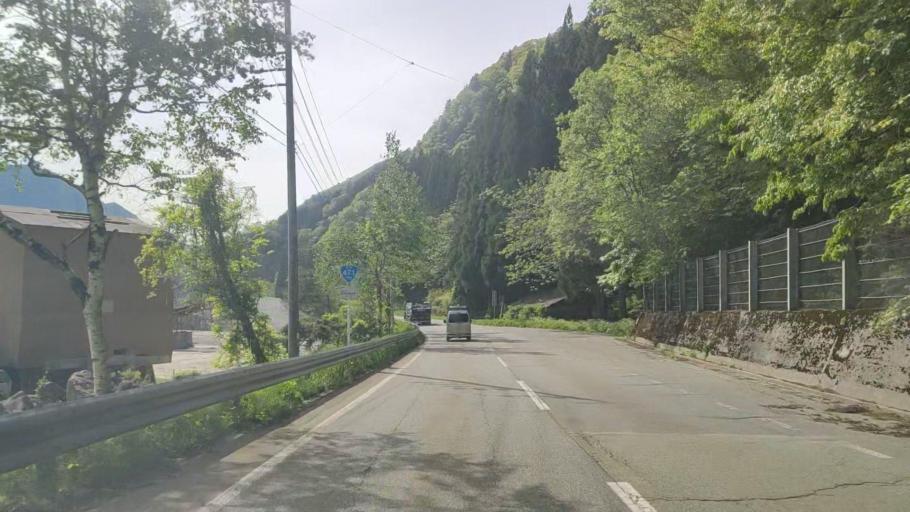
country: JP
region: Gifu
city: Takayama
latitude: 36.2594
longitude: 137.4560
